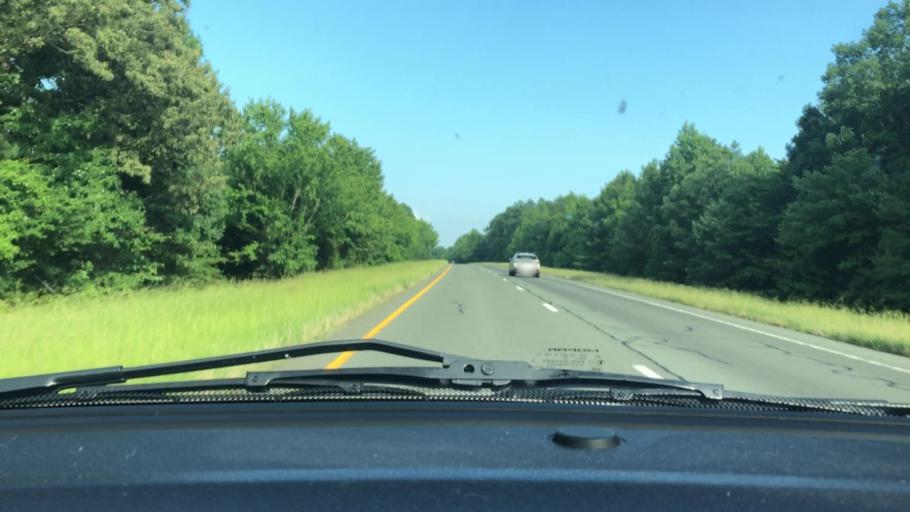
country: US
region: North Carolina
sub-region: Randolph County
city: Liberty
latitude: 35.7872
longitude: -79.5221
